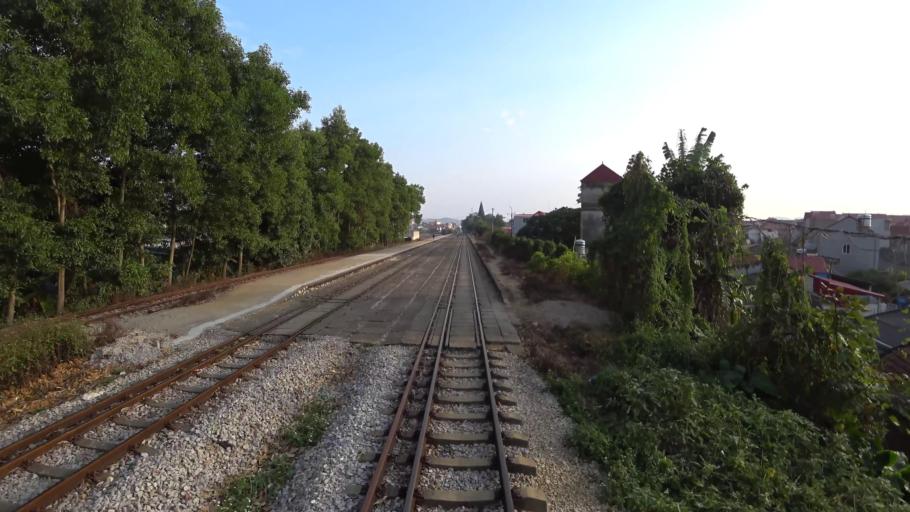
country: VN
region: Lang Son
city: Thi Tran Cao Loc
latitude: 21.8684
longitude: 106.7621
